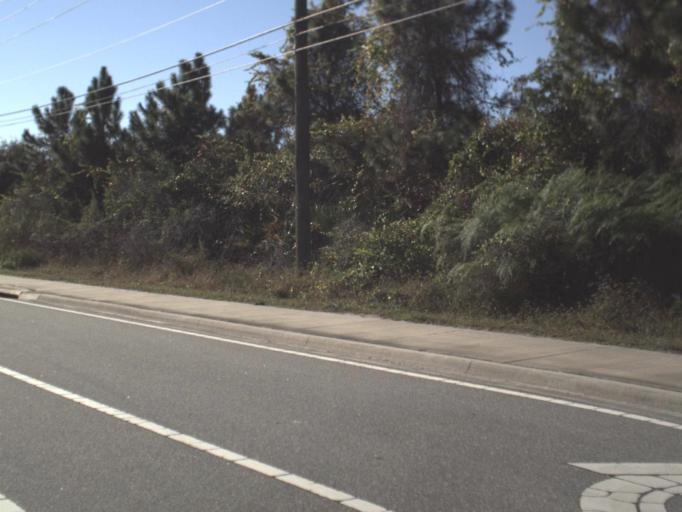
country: US
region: Florida
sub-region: Volusia County
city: Holly Hill
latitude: 29.2288
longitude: -81.0872
